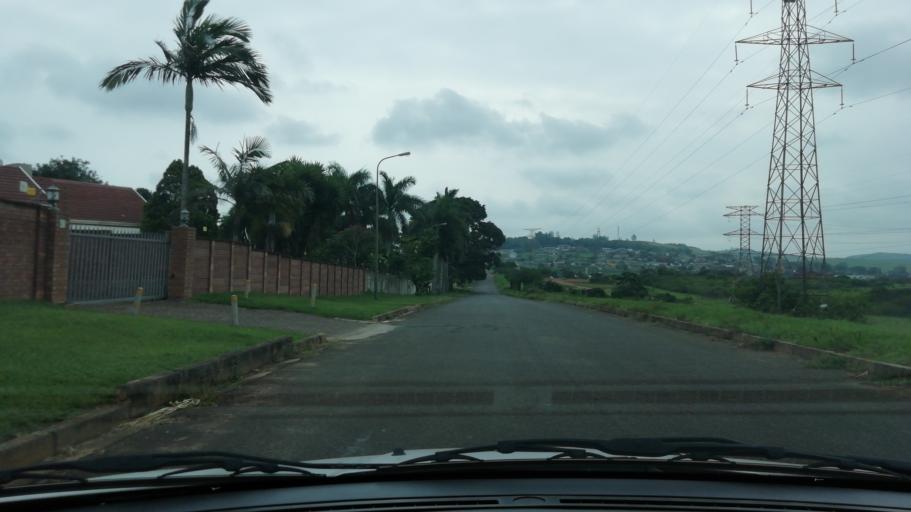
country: ZA
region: KwaZulu-Natal
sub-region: uThungulu District Municipality
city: Empangeni
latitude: -28.7368
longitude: 31.8901
